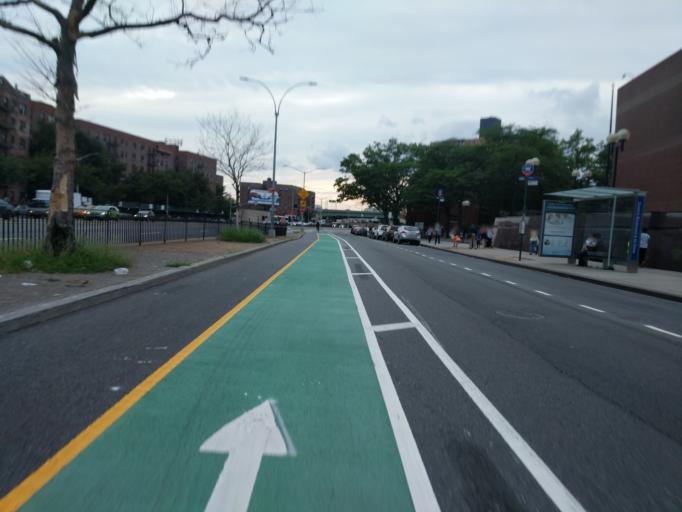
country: US
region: New York
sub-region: Queens County
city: Borough of Queens
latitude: 40.7312
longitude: -73.8646
